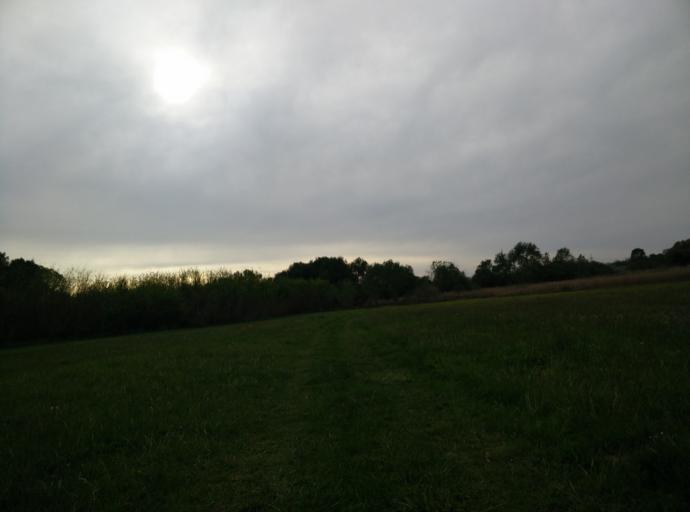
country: HU
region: Pest
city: Fot
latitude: 47.6072
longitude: 19.1787
